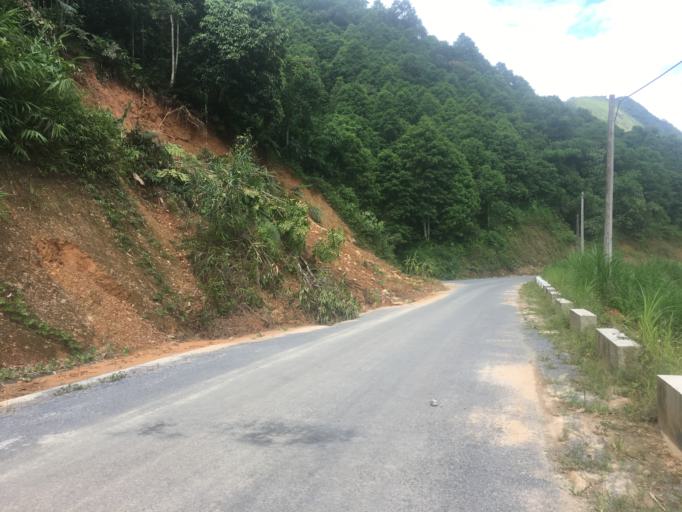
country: VN
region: Ha Giang
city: Thanh Pho Ha Giang
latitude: 22.8562
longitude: 105.0426
